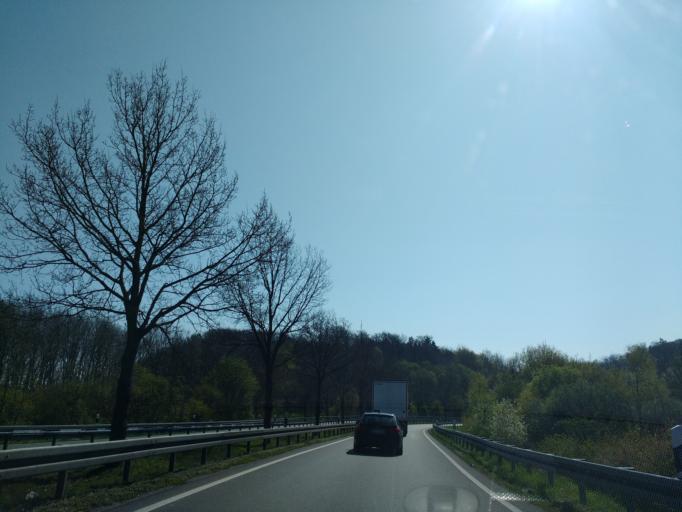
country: DE
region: Lower Saxony
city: Osnabrueck
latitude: 52.2468
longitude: 8.0893
